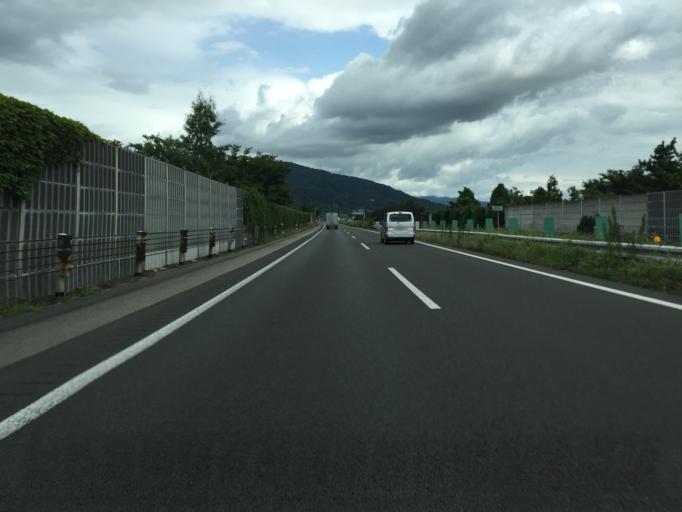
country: JP
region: Fukushima
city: Fukushima-shi
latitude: 37.8118
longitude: 140.4696
